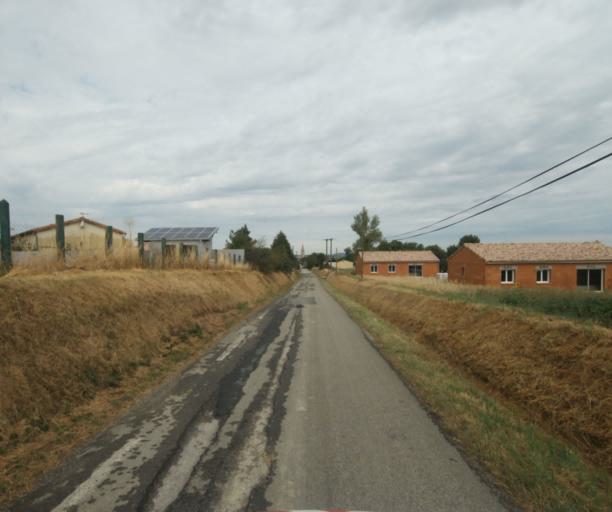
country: FR
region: Midi-Pyrenees
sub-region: Departement de la Haute-Garonne
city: Revel
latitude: 43.4333
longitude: 1.9725
